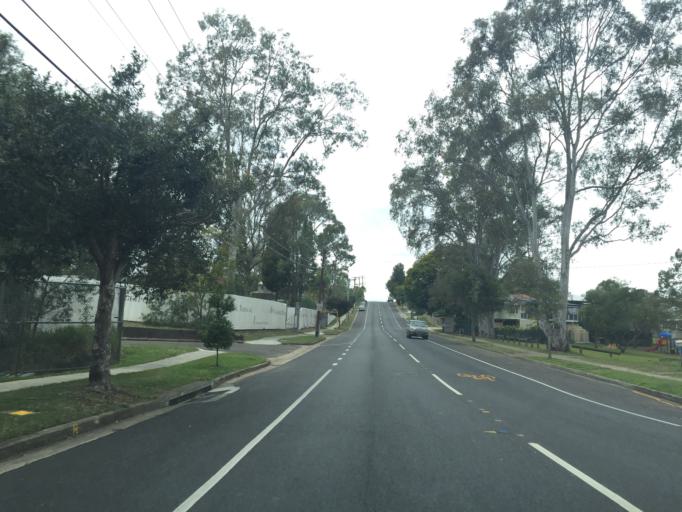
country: AU
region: Queensland
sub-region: Brisbane
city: Everton Park
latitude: -27.4377
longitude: 152.9809
